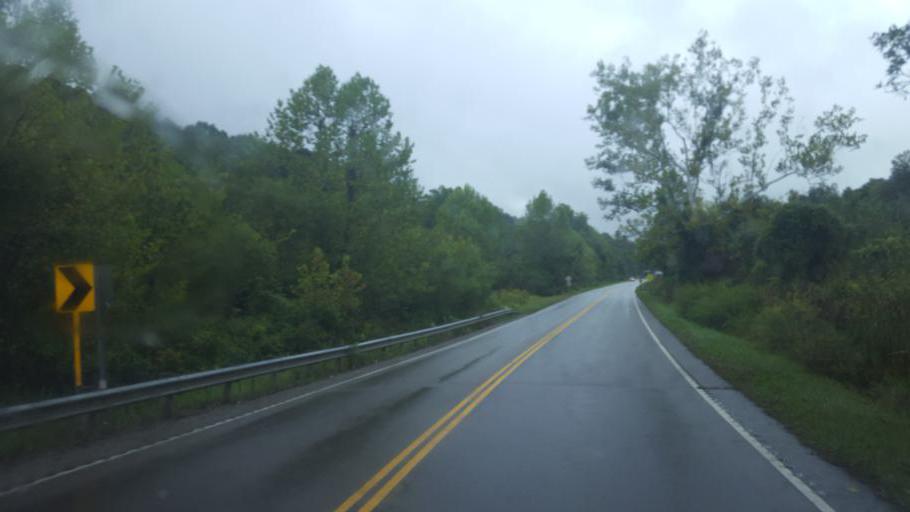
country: US
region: Ohio
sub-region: Jackson County
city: Oak Hill
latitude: 38.8351
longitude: -82.6481
